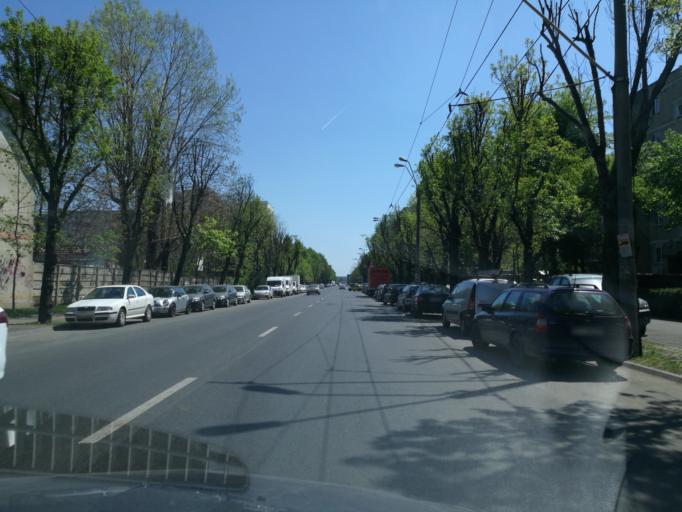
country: RO
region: Ilfov
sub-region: Comuna Popesti-Leordeni
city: Popesti-Leordeni
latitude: 44.3843
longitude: 26.1229
